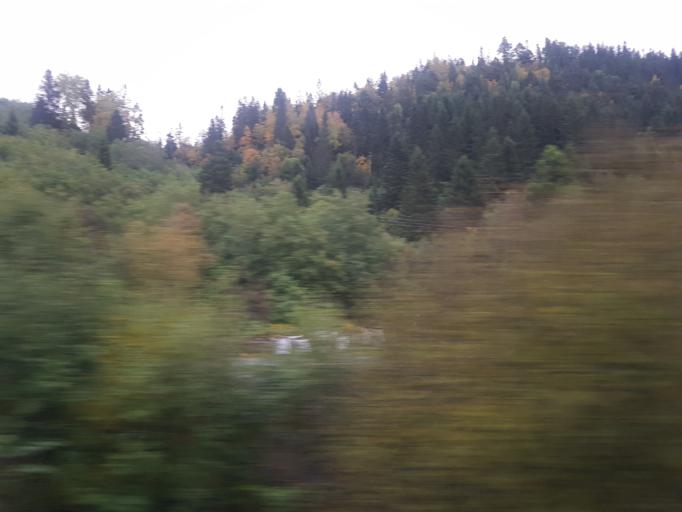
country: NO
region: Sor-Trondelag
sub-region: Melhus
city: Melhus
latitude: 63.2223
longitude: 10.2869
